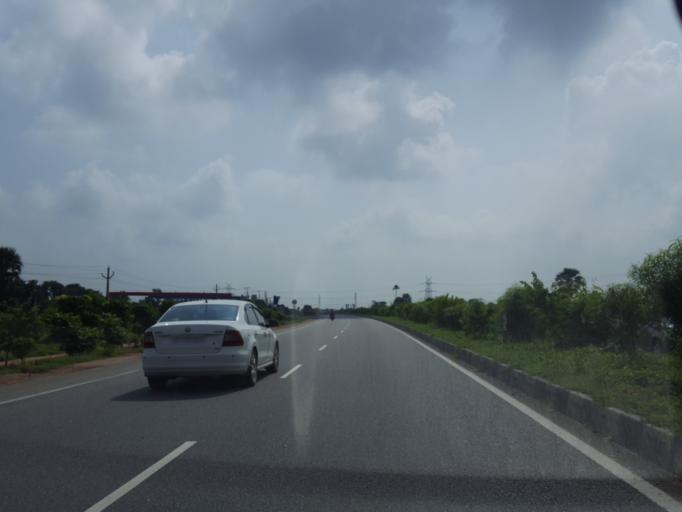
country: IN
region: Telangana
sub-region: Nalgonda
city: Gudur
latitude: 17.2652
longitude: 78.8318
